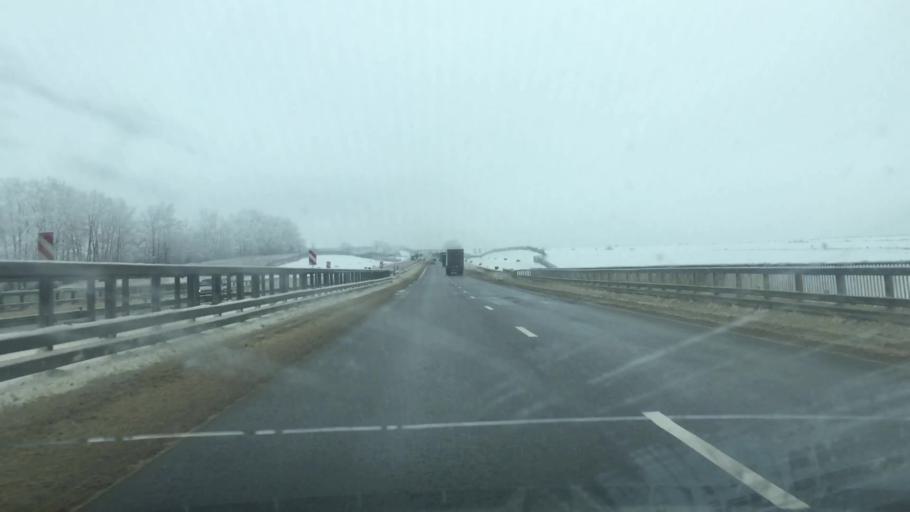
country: RU
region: Tula
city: Kazachka
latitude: 53.3297
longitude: 38.1803
